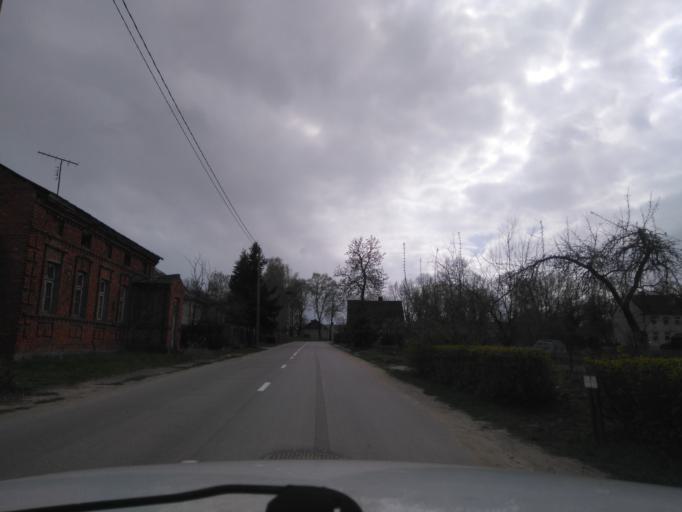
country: LT
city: Virbalis
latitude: 54.6278
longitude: 22.8235
